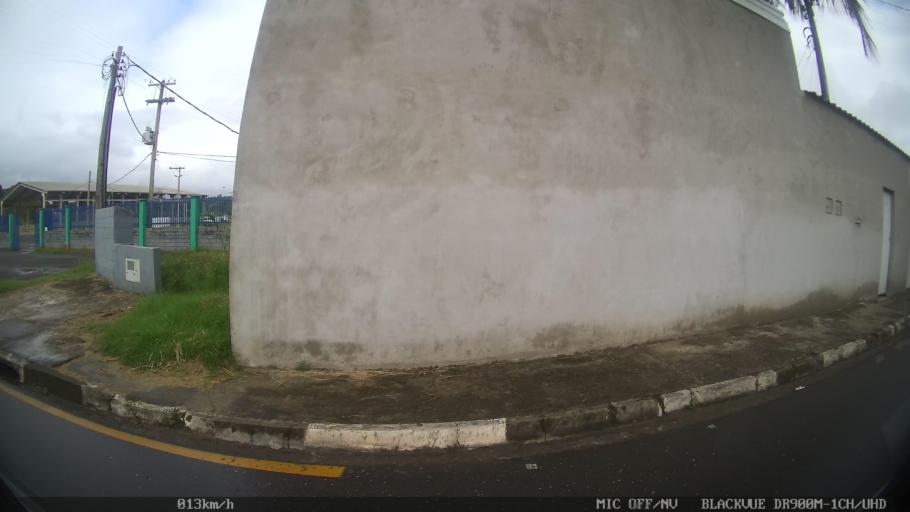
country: BR
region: Sao Paulo
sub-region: Cajati
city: Cajati
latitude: -24.7242
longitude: -48.1029
